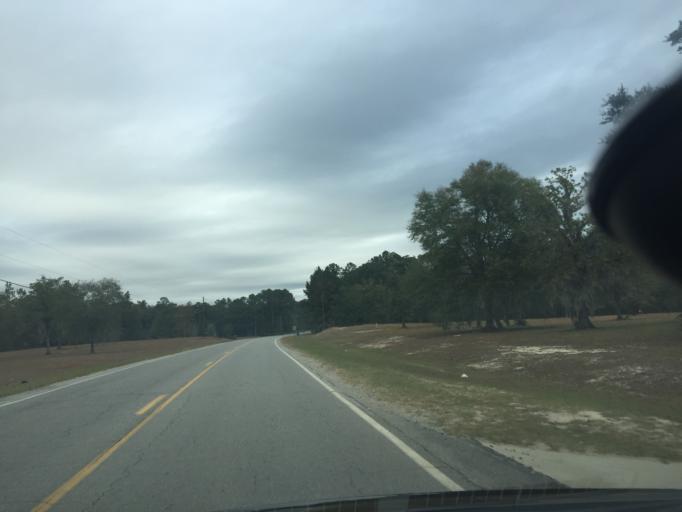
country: US
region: Georgia
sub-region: Chatham County
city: Bloomingdale
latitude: 32.1032
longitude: -81.3829
